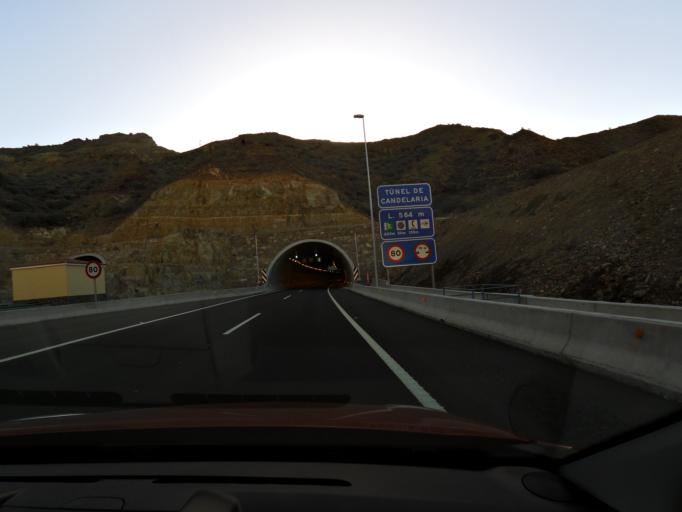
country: ES
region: Canary Islands
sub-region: Provincia de Las Palmas
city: Puerto Rico
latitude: 27.8073
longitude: -15.7122
